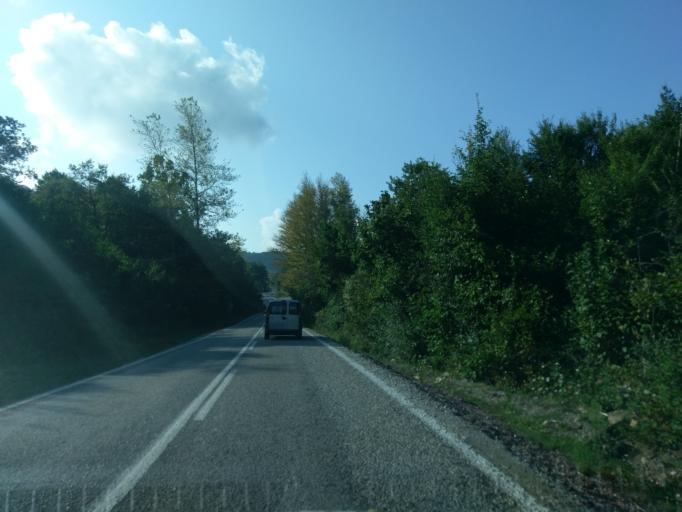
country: TR
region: Sinop
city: Ayancik
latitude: 41.8812
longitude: 34.5247
